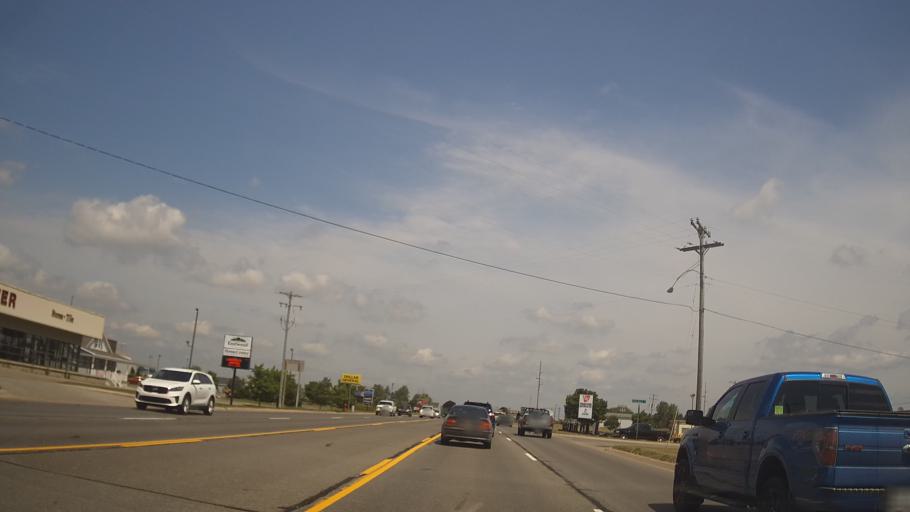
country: US
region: Michigan
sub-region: Grand Traverse County
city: Traverse City
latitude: 44.6762
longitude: -85.6563
